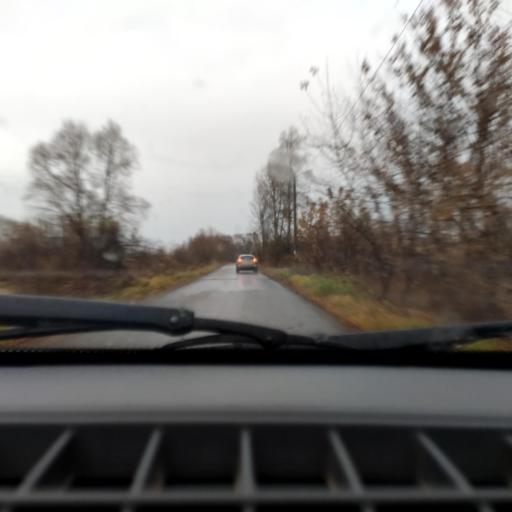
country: RU
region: Bashkortostan
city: Avdon
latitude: 54.6464
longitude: 55.7499
